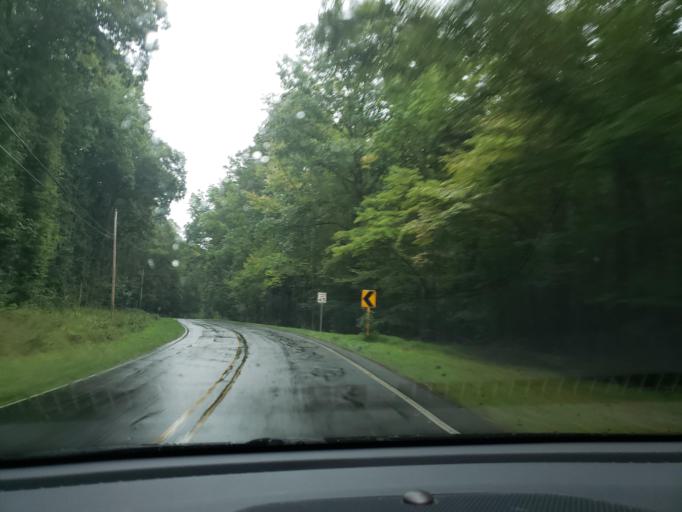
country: US
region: North Carolina
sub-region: Orange County
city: Chapel Hill
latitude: 35.9917
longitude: -79.0052
